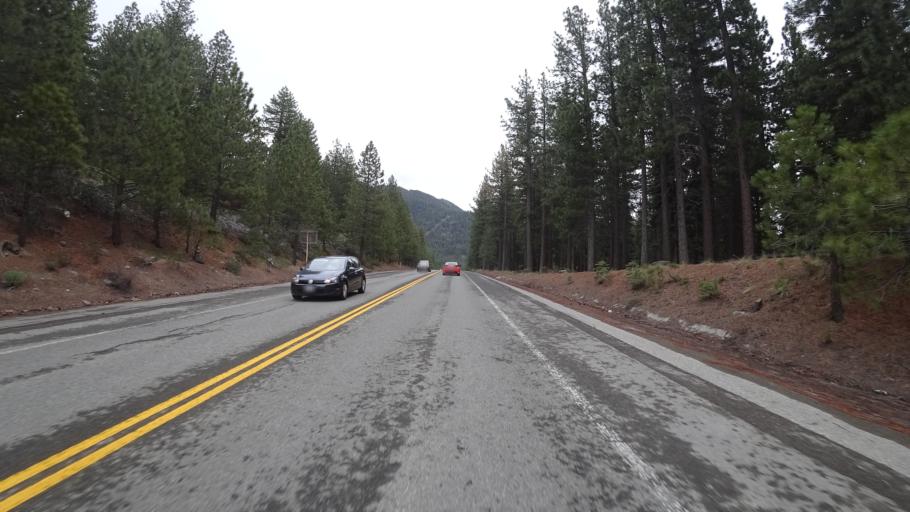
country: US
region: Nevada
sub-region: Washoe County
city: Incline Village
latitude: 39.2439
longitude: -119.9354
